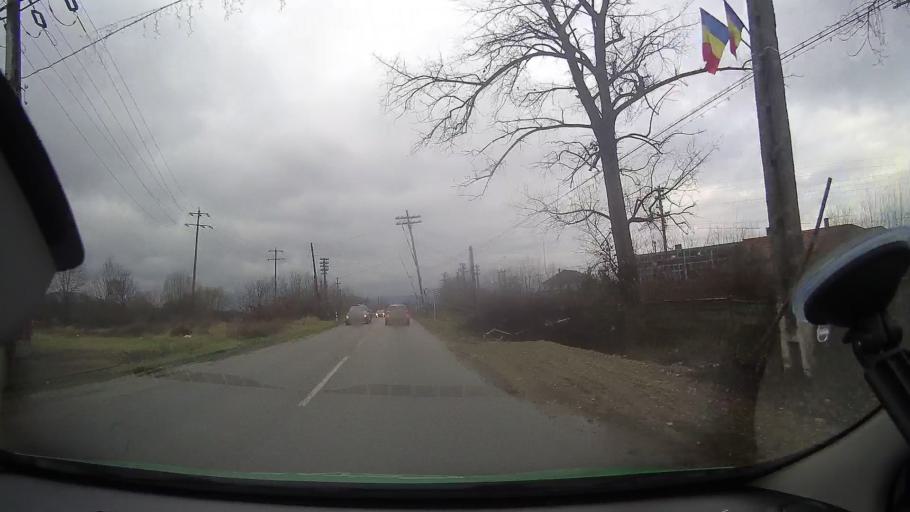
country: RO
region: Arad
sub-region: Comuna Sebis
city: Sebis
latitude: 46.3619
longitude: 22.1307
